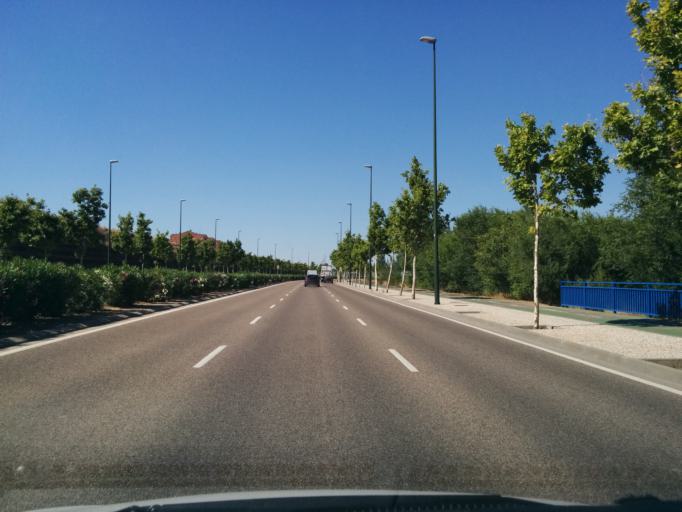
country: ES
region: Aragon
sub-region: Provincia de Zaragoza
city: Zaragoza
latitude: 41.6413
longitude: -0.8580
